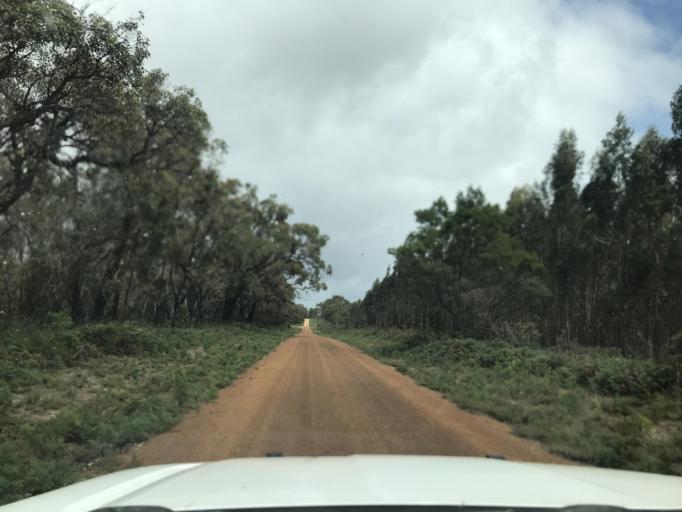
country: AU
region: South Australia
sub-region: Wattle Range
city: Penola
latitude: -37.2932
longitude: 141.2982
